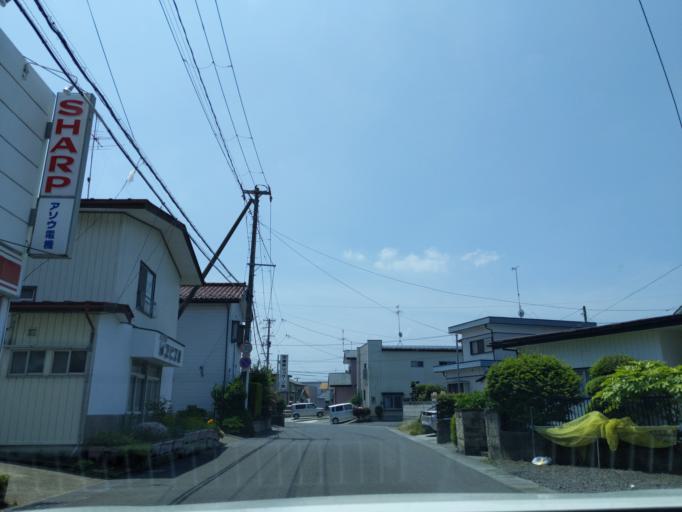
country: JP
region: Fukushima
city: Koriyama
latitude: 37.3708
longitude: 140.3571
